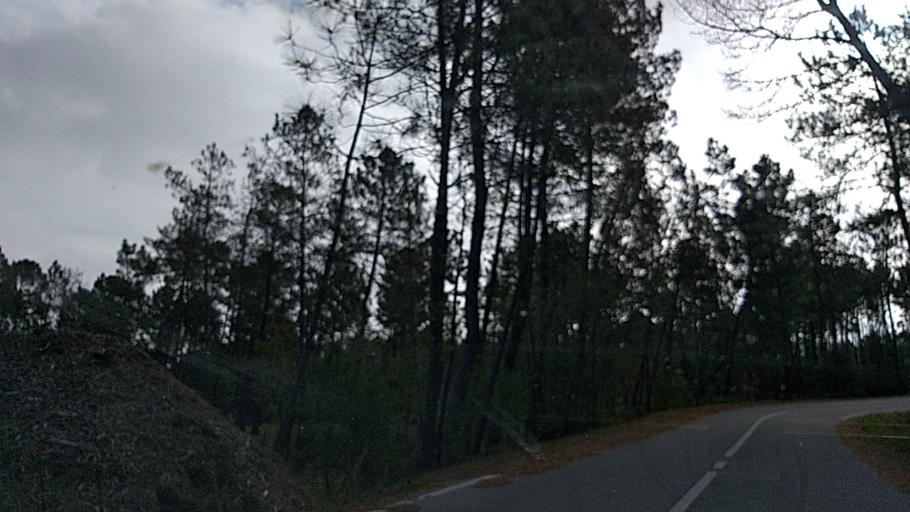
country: PT
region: Guarda
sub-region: Fornos de Algodres
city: Fornos de Algodres
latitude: 40.6969
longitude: -7.5597
